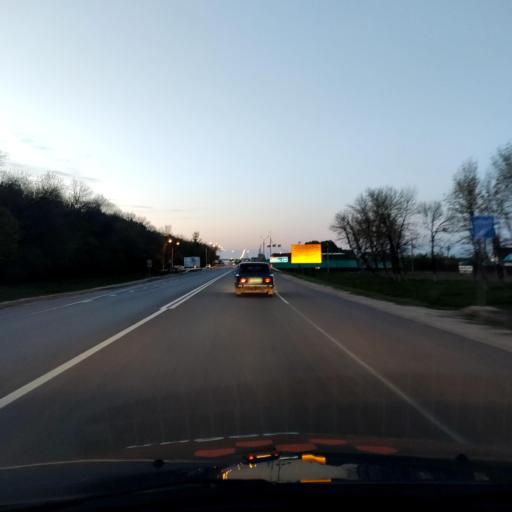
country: RU
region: Orjol
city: Zmiyevka
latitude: 52.7051
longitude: 36.3656
